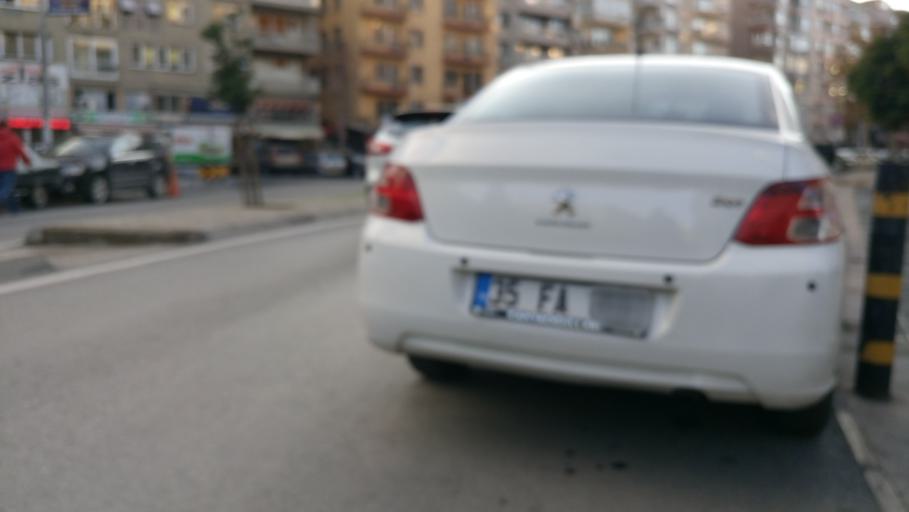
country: TR
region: Izmir
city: Izmir
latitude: 38.4071
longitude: 27.1068
